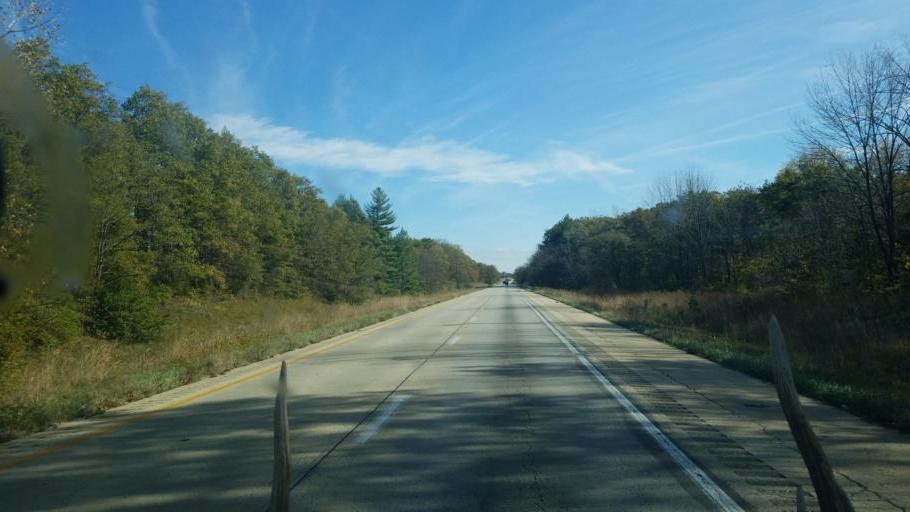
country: US
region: Illinois
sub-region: Effingham County
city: Effingham
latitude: 39.0776
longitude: -88.6376
